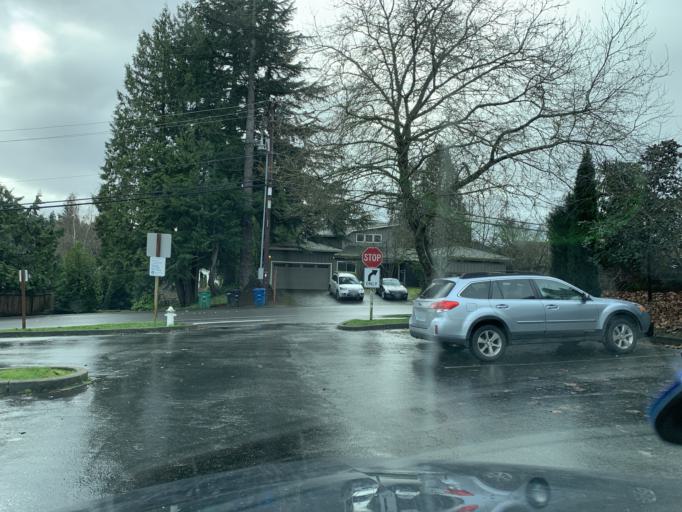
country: US
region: Washington
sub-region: King County
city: Mercer Island
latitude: 47.5893
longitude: -122.2288
